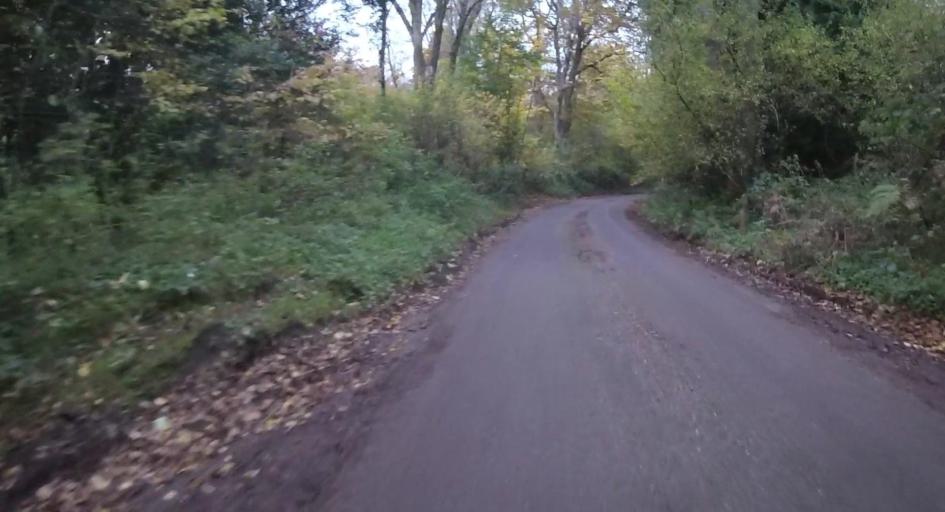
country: GB
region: England
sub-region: Hampshire
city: Lindford
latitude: 51.1323
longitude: -0.8132
